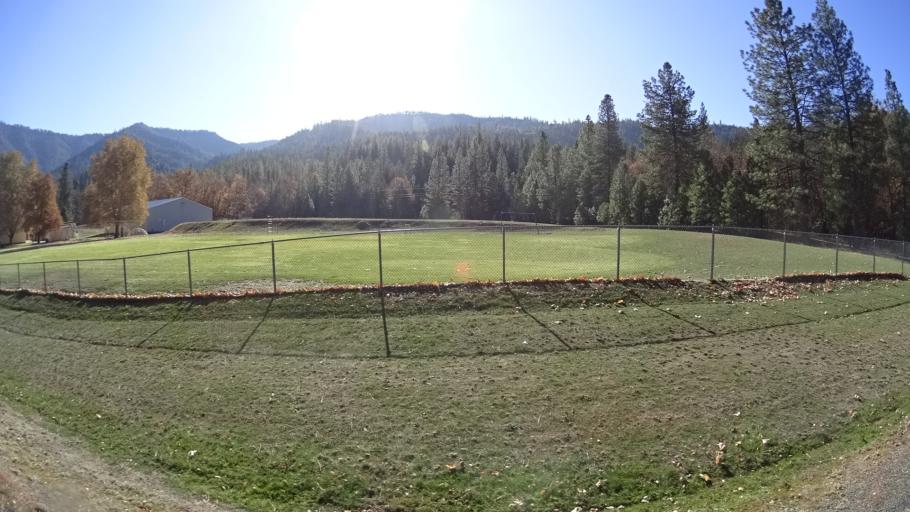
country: US
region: California
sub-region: Siskiyou County
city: Yreka
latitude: 41.8225
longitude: -122.9708
